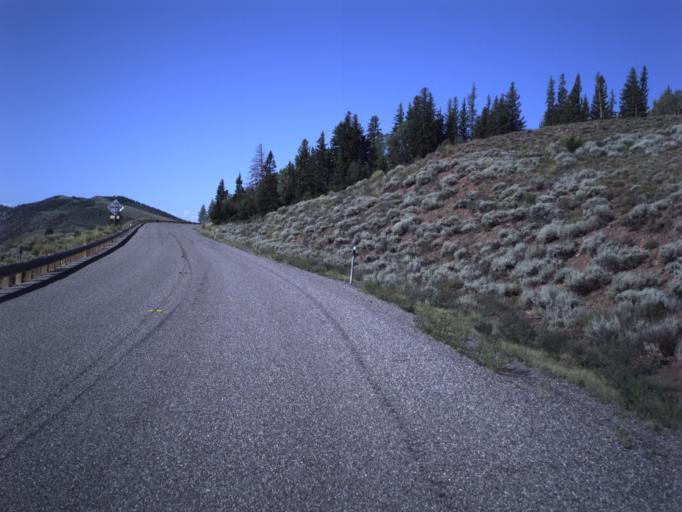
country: US
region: Utah
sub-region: Wayne County
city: Loa
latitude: 38.5959
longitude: -111.4693
